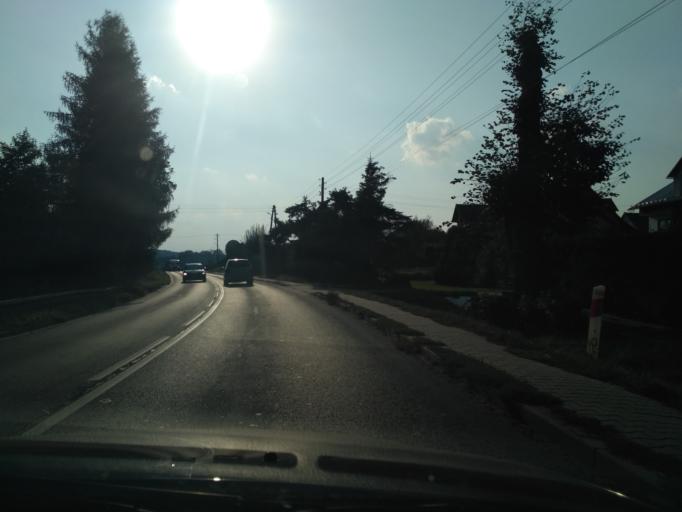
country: PL
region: Subcarpathian Voivodeship
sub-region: Powiat strzyzowski
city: Czudec
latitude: 49.9449
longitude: 21.8241
